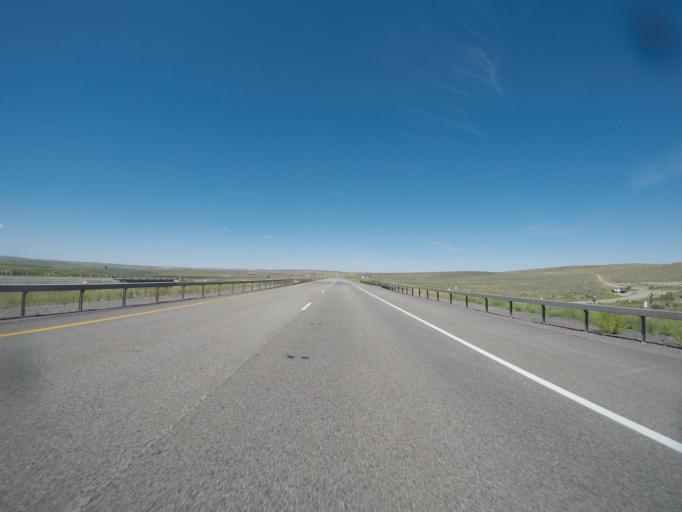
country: US
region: Wyoming
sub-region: Carbon County
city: Saratoga
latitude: 41.7433
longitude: -106.7732
